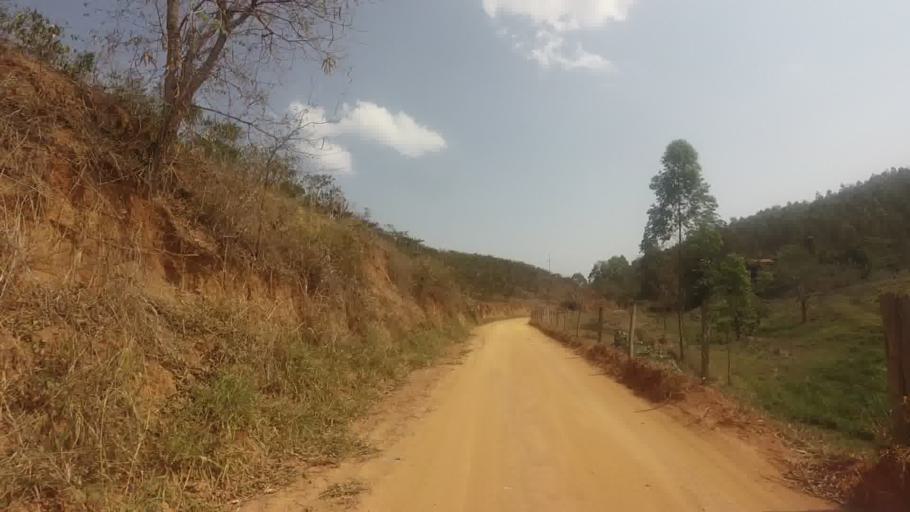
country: BR
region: Espirito Santo
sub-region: Sao Jose Do Calcado
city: Sao Jose do Calcado
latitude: -21.0503
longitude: -41.5264
